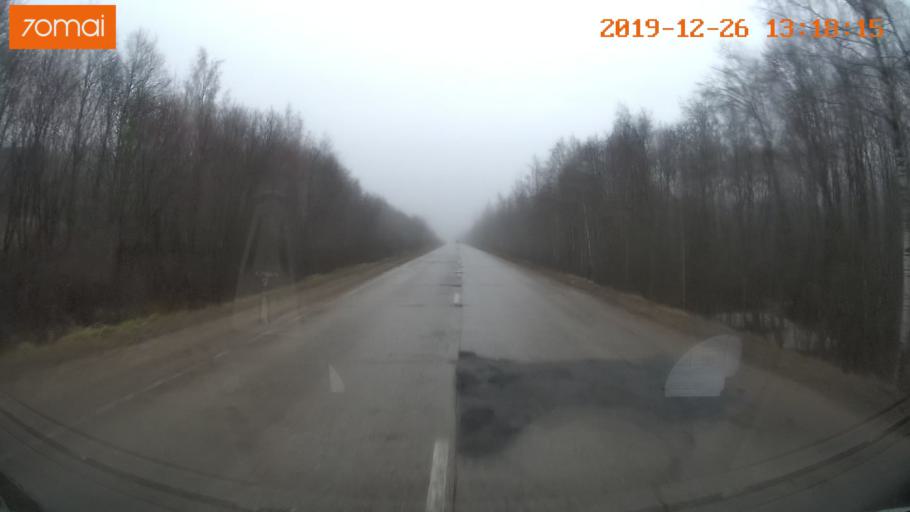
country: RU
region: Vologda
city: Cherepovets
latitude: 58.9576
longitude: 38.1209
